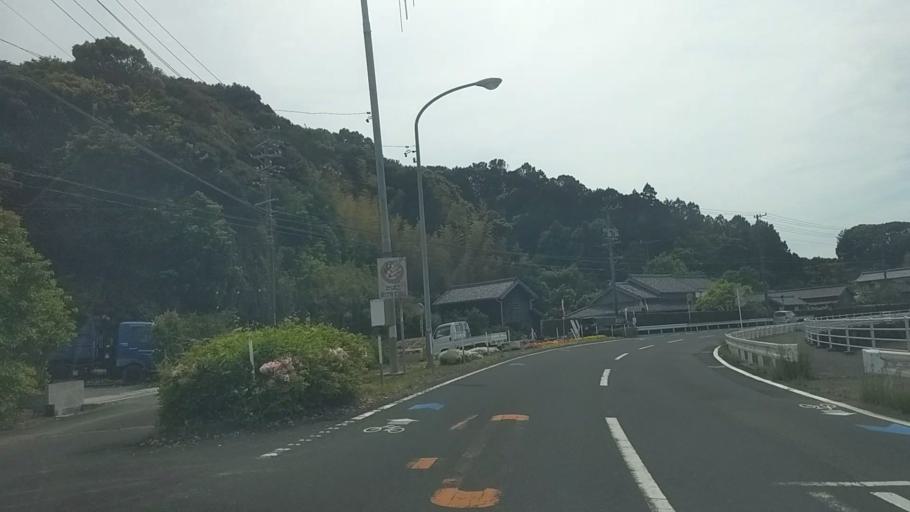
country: JP
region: Shizuoka
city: Hamamatsu
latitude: 34.7832
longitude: 137.6424
